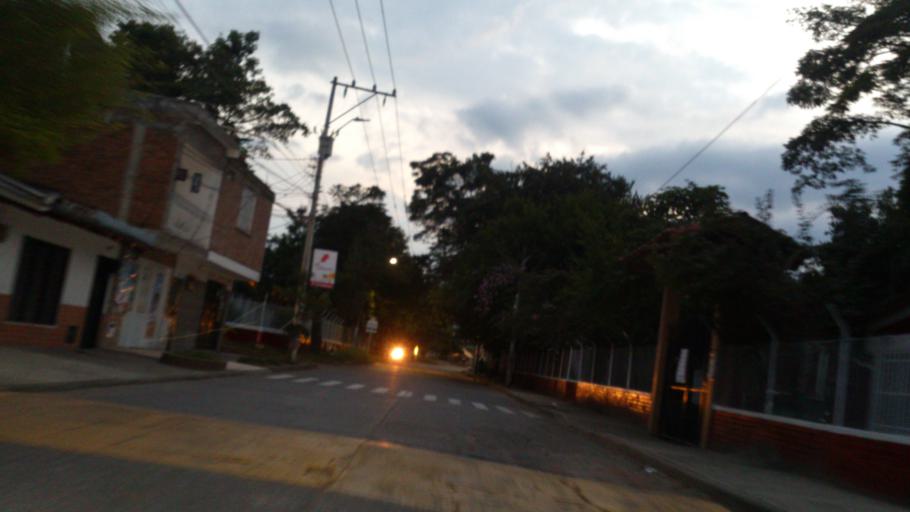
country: CO
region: Valle del Cauca
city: Jamundi
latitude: 3.2656
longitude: -76.5417
